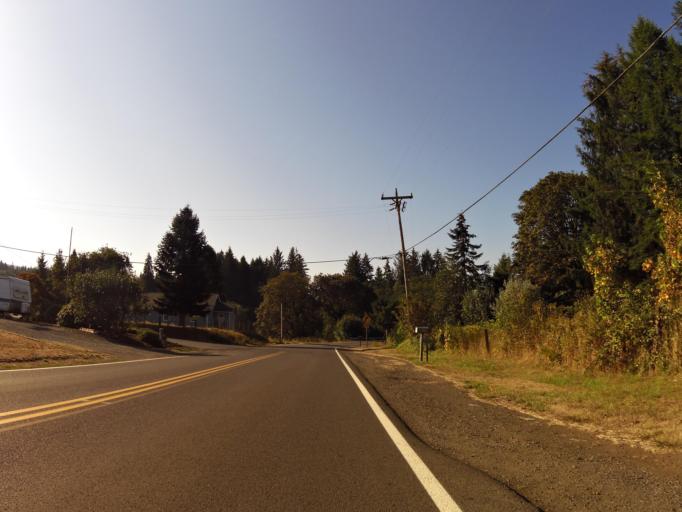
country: US
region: Oregon
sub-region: Tillamook County
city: Tillamook
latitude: 45.3873
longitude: -123.7948
